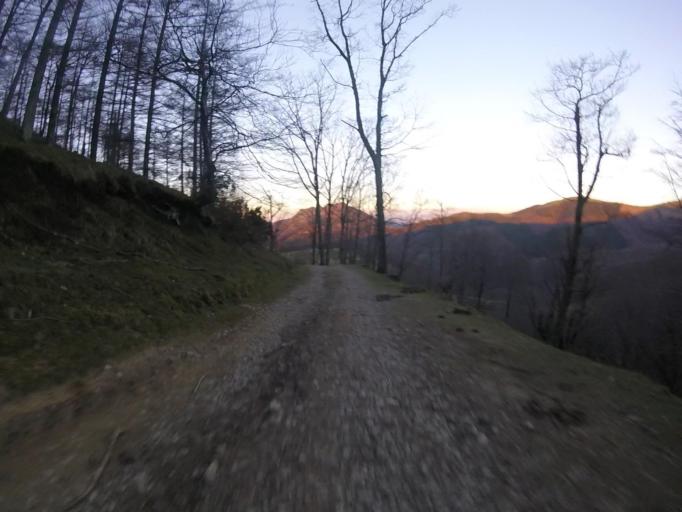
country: ES
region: Basque Country
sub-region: Provincia de Guipuzcoa
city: Irun
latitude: 43.2585
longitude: -1.8266
